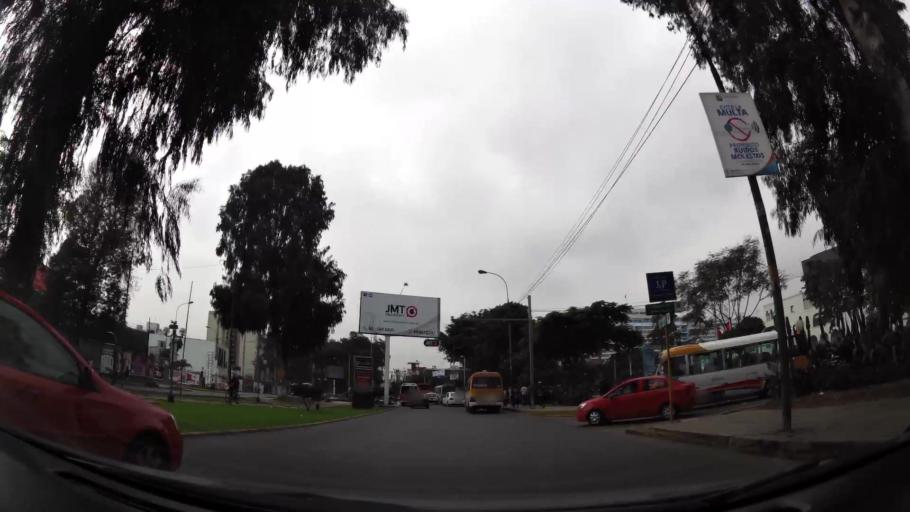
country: PE
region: Lima
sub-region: Lima
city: San Isidro
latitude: -12.0805
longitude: -77.0423
